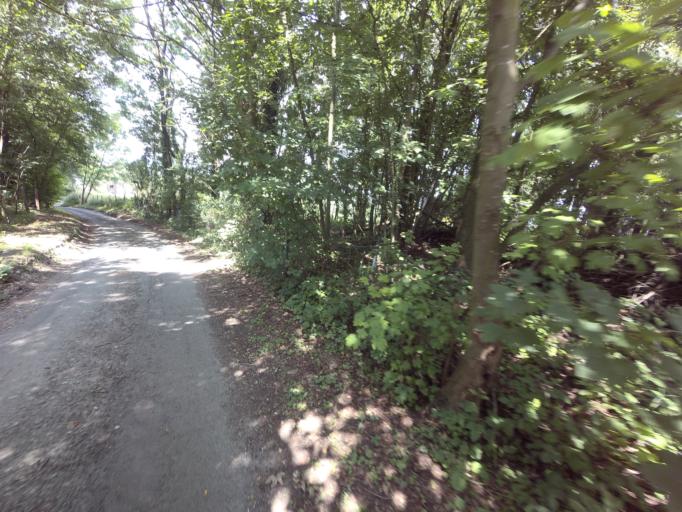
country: BE
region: Wallonia
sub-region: Province de Liege
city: Lontzen
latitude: 50.6973
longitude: 5.9866
